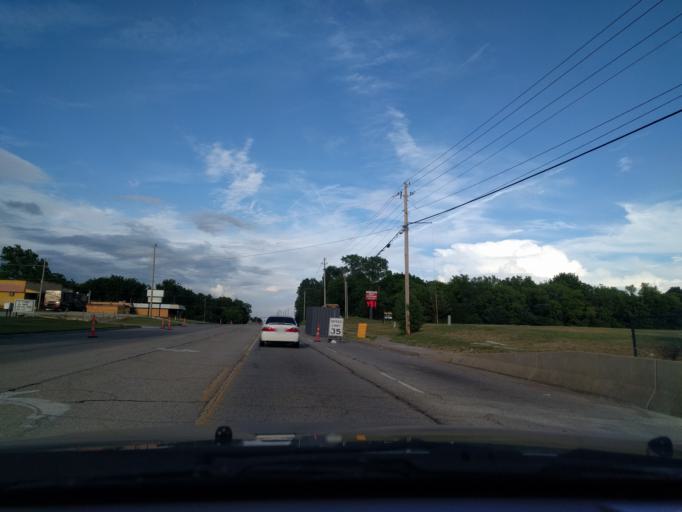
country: US
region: Oklahoma
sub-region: Tulsa County
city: Broken Arrow
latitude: 36.0608
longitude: -95.8389
